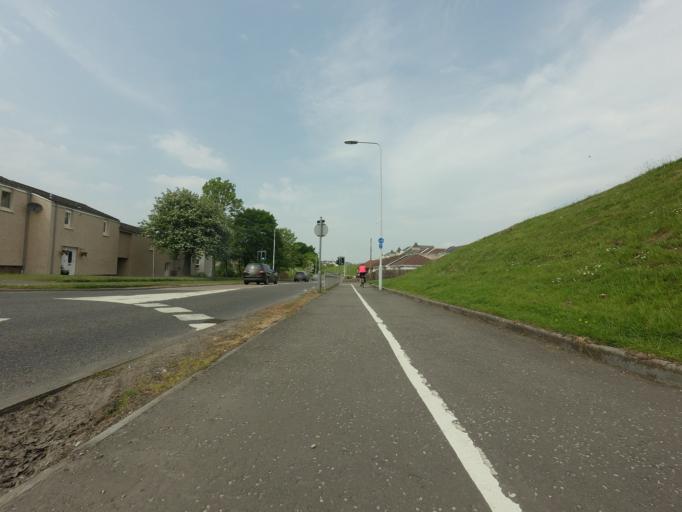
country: GB
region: Scotland
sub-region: Fife
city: Townhill
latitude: 56.0619
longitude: -3.4148
